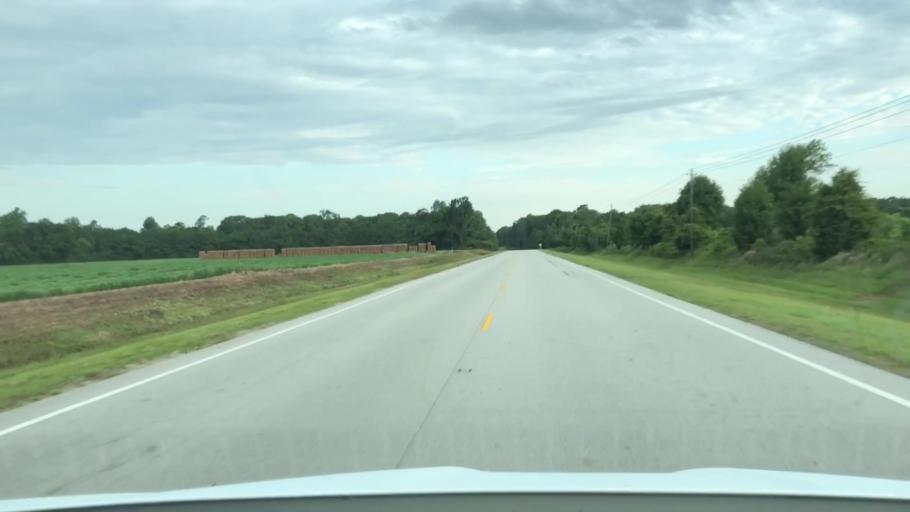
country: US
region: North Carolina
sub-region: Jones County
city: Trenton
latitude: 35.0030
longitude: -77.2765
